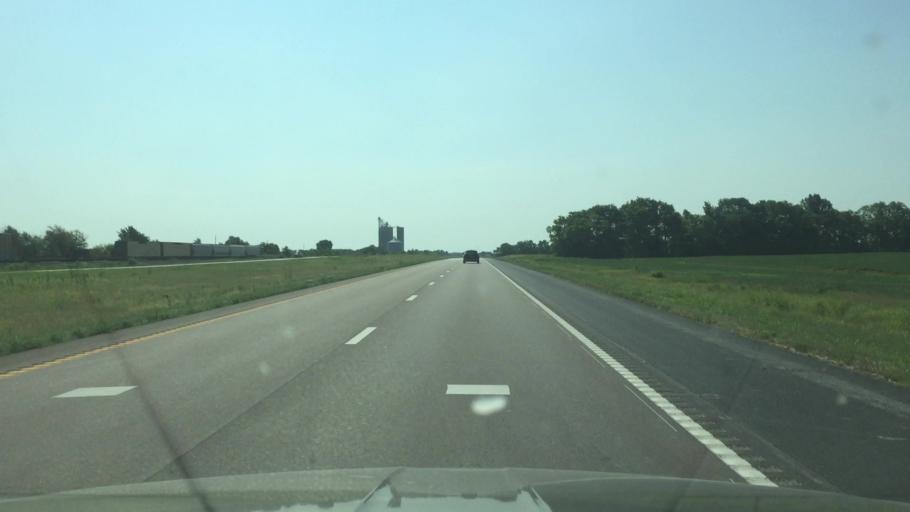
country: US
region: Missouri
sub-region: Pettis County
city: La Monte
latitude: 38.7557
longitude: -93.3621
